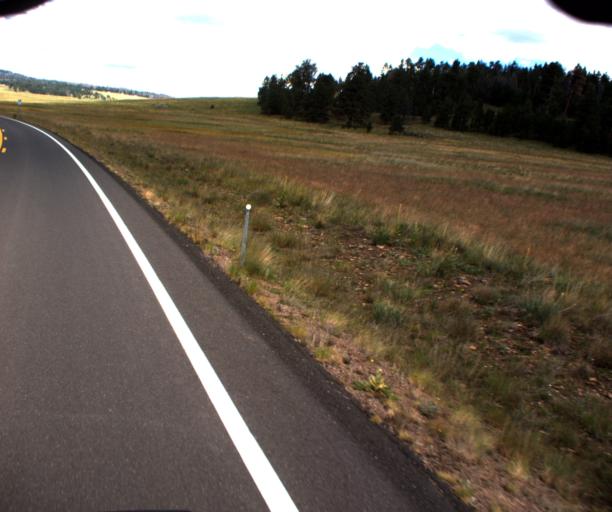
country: US
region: Arizona
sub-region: Apache County
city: Eagar
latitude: 33.9141
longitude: -109.4174
